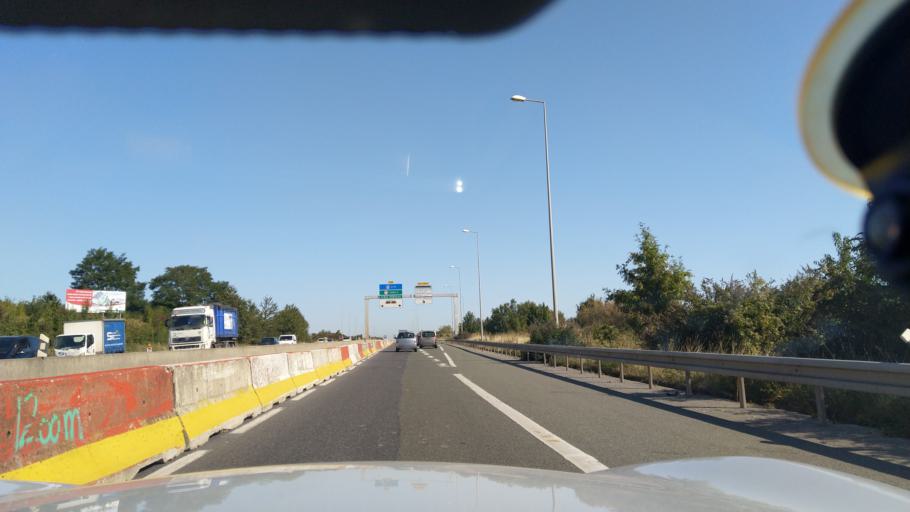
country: FR
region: Ile-de-France
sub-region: Departement du Val-d'Oise
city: Le Thillay
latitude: 49.0070
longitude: 2.4901
